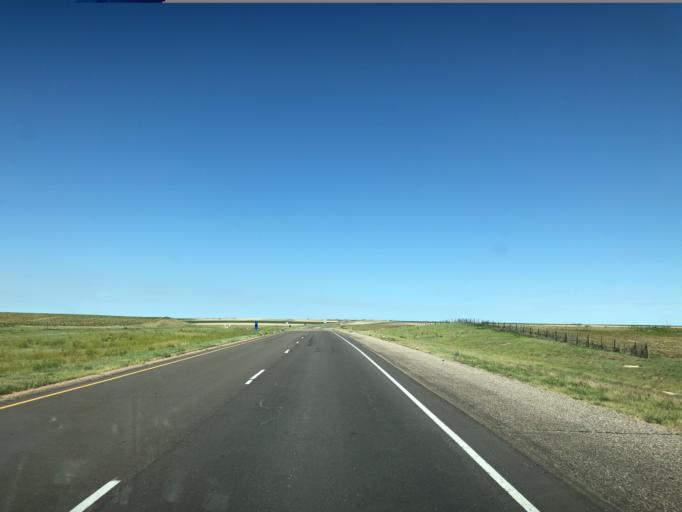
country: US
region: Colorado
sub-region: Kit Carson County
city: Burlington
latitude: 39.2941
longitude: -102.4378
